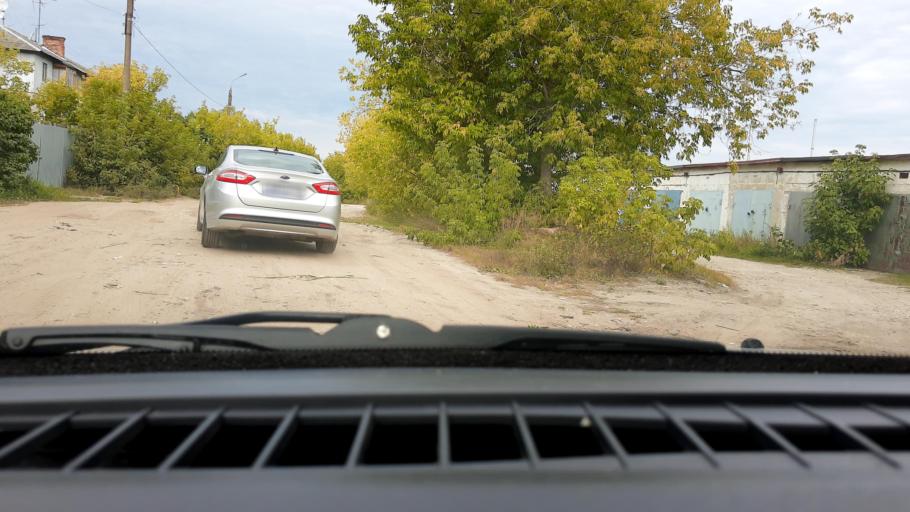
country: RU
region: Nizjnij Novgorod
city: Dzerzhinsk
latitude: 56.2475
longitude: 43.4803
